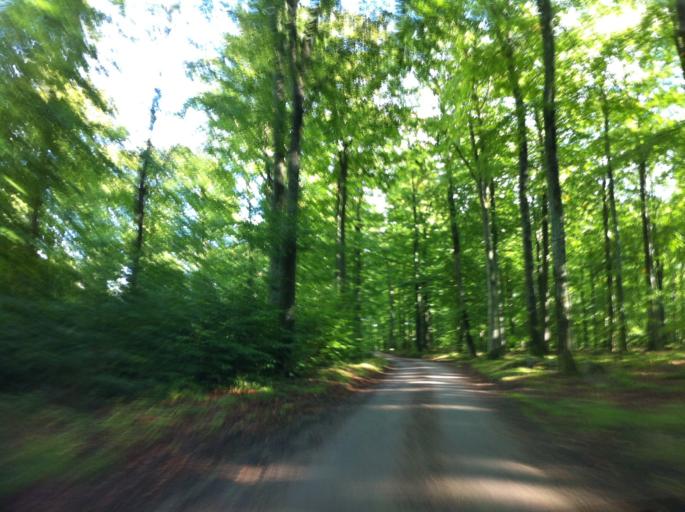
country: SE
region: Skane
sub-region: Hassleholms Kommun
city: Sosdala
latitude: 56.1324
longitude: 13.5776
